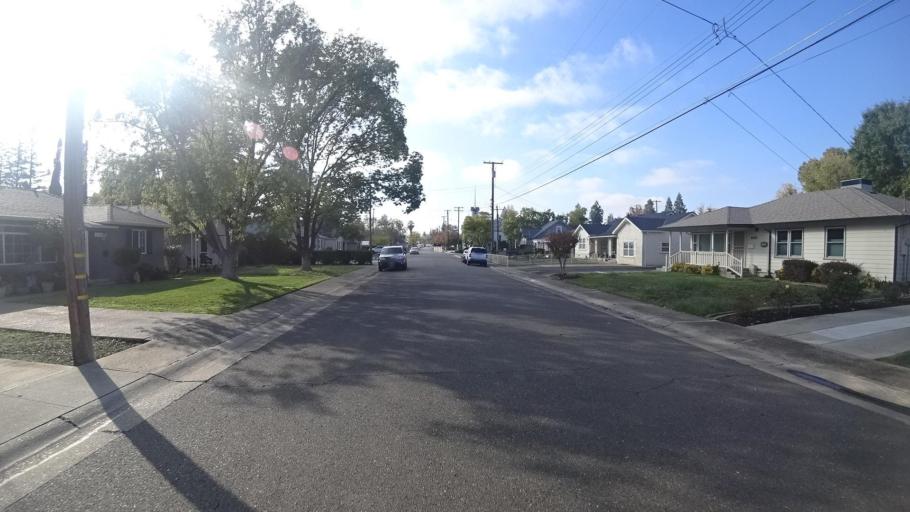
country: US
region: California
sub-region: Sacramento County
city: Elk Grove
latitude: 38.4101
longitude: -121.3597
